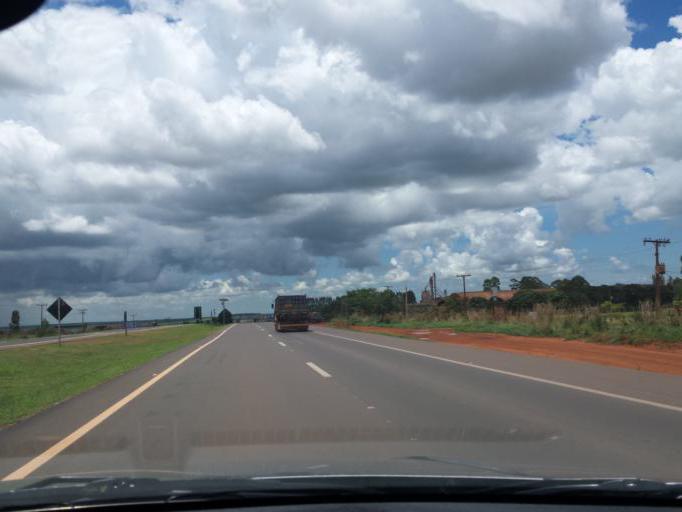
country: BR
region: Goias
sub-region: Cristalina
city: Cristalina
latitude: -16.7799
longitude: -47.6290
